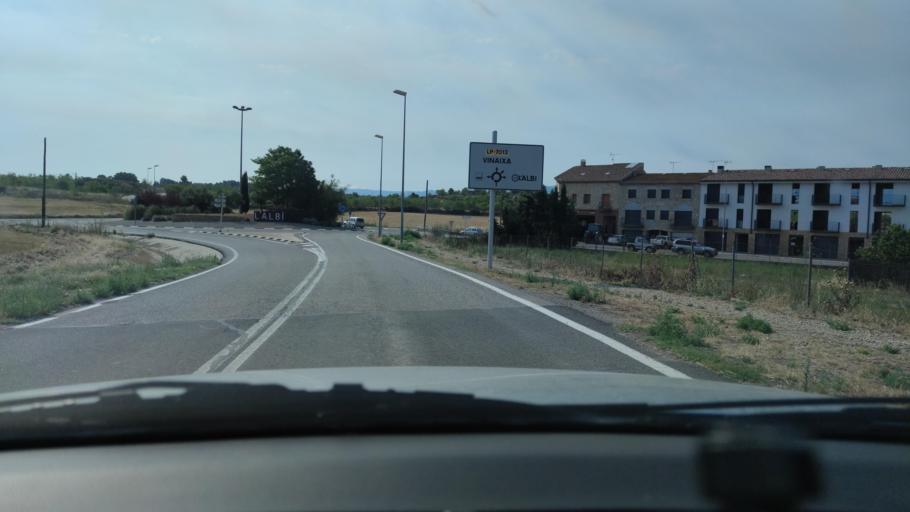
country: ES
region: Catalonia
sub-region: Provincia de Lleida
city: Vinaixa
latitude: 41.4245
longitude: 0.9433
